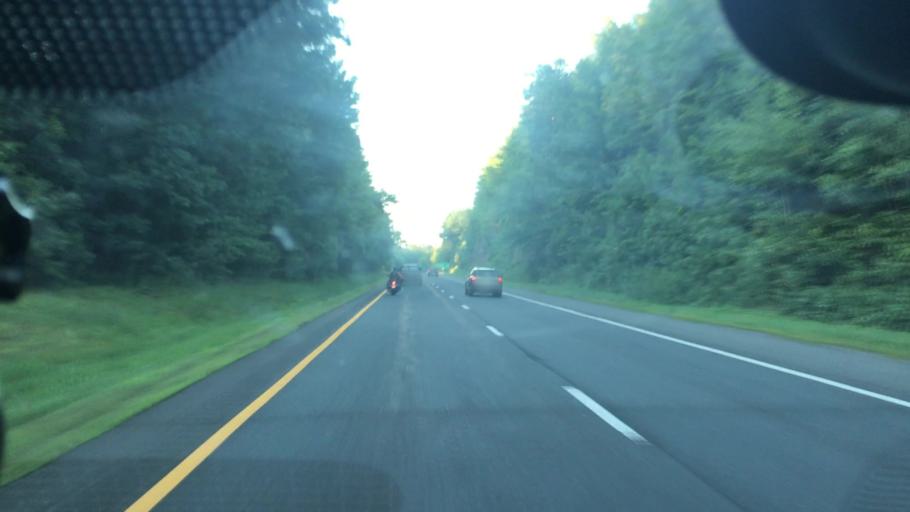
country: US
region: Massachusetts
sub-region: Franklin County
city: Turners Falls
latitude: 42.6268
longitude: -72.5841
